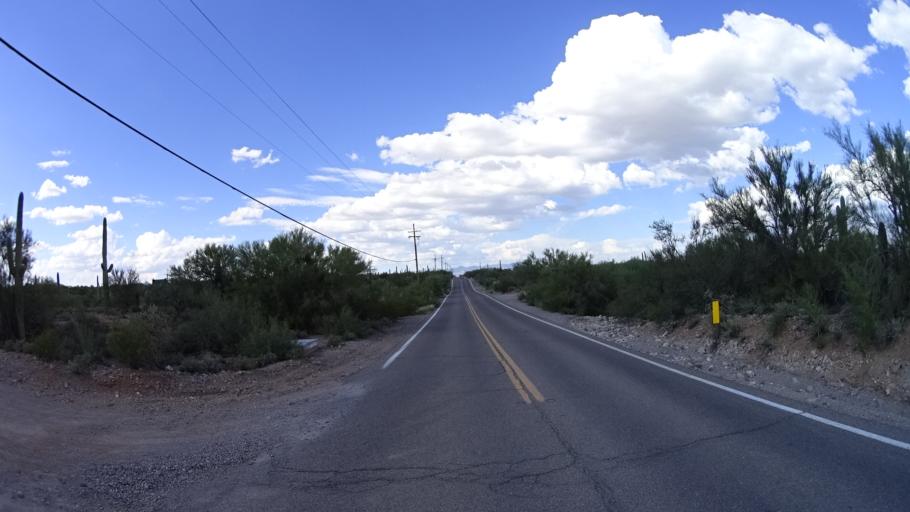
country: US
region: Arizona
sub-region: Pima County
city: Flowing Wells
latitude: 32.2672
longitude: -111.0628
